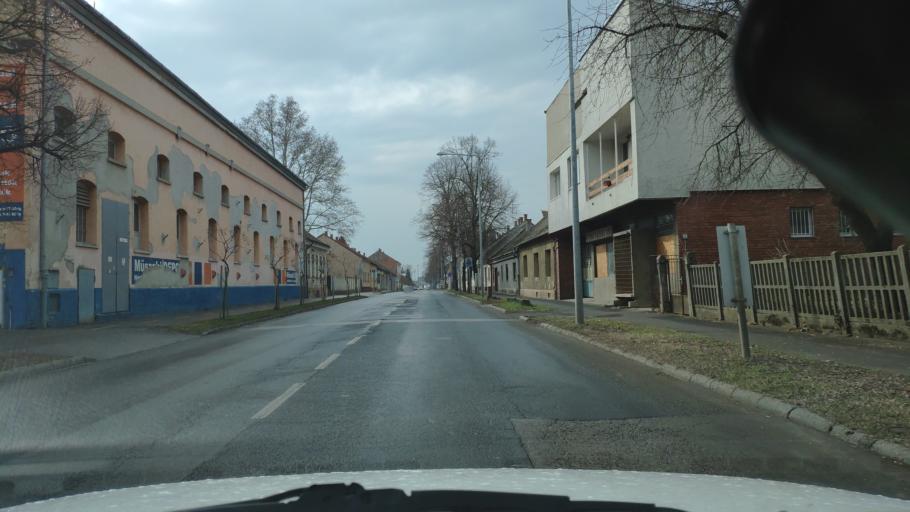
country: HU
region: Zala
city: Nagykanizsa
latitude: 46.4484
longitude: 16.9915
